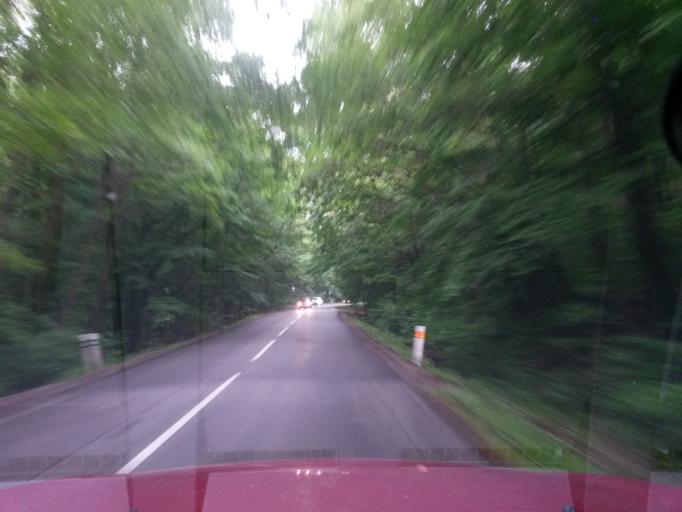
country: SK
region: Kosicky
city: Kosice
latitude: 48.6756
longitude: 21.1585
